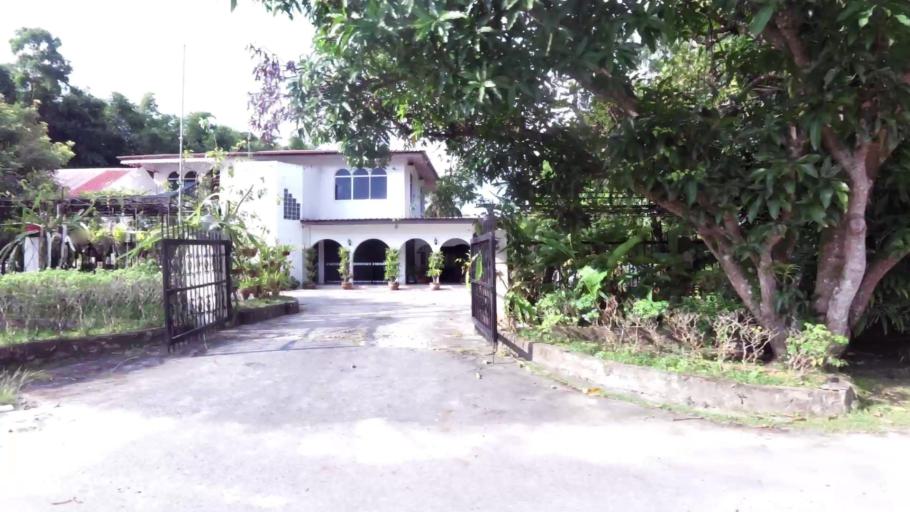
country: BN
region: Brunei and Muara
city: Bandar Seri Begawan
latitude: 4.9653
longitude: 114.9749
